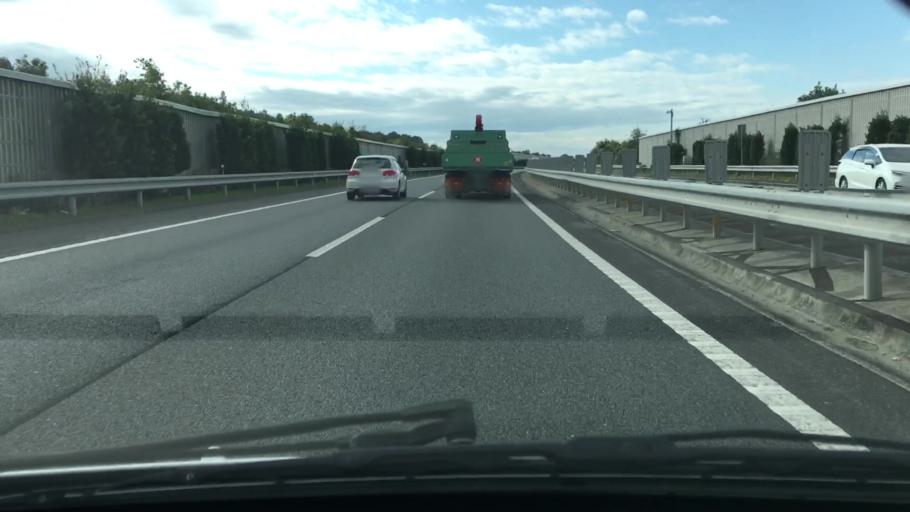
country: JP
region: Chiba
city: Ichihara
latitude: 35.5406
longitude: 140.1393
